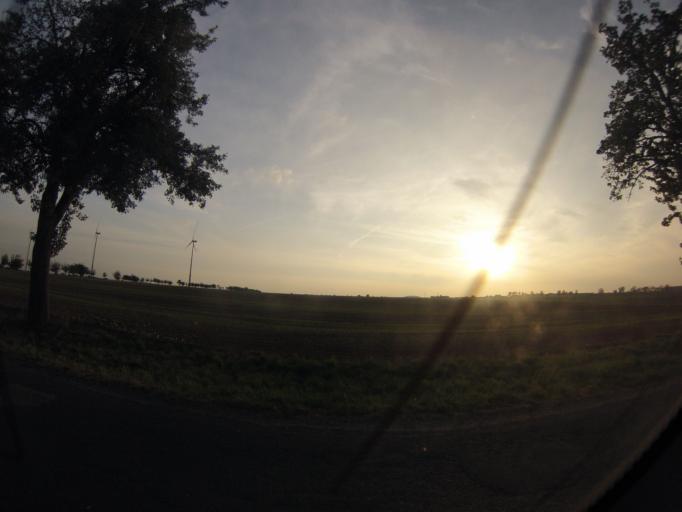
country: DE
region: Thuringia
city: Drogen
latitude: 50.9157
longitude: 12.3060
